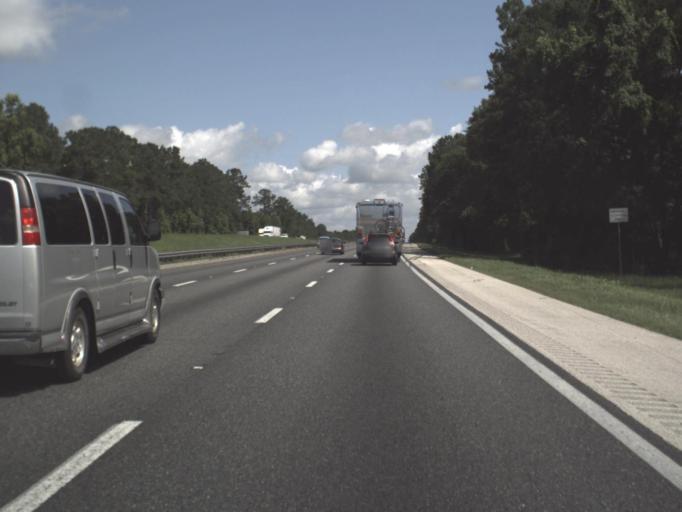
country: US
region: Florida
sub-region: Alachua County
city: Alachua
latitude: 29.7023
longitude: -82.4581
